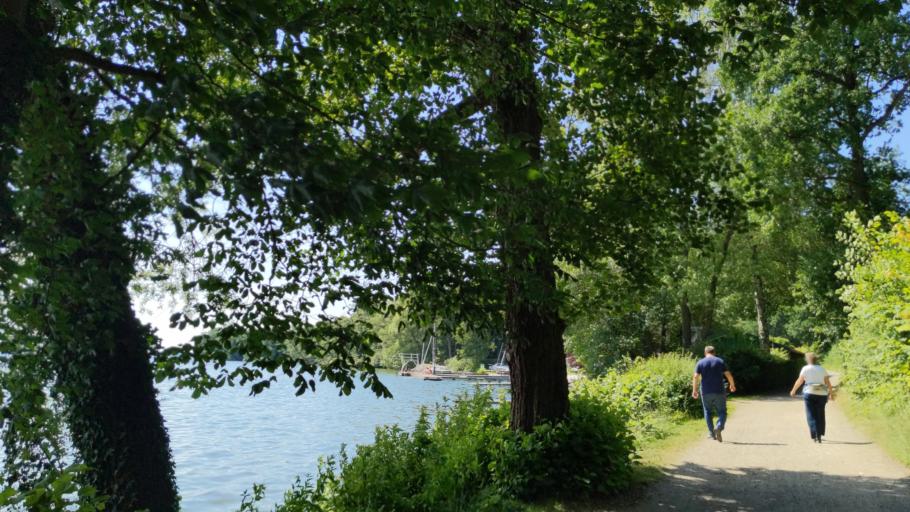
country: DE
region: Schleswig-Holstein
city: Ploen
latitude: 54.1526
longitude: 10.4093
